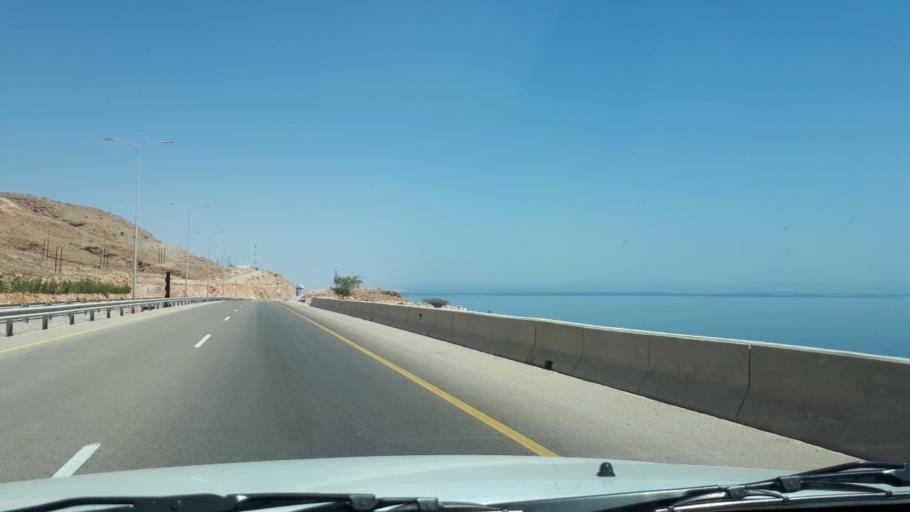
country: OM
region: Ash Sharqiyah
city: Sur
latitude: 22.8305
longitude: 59.2506
